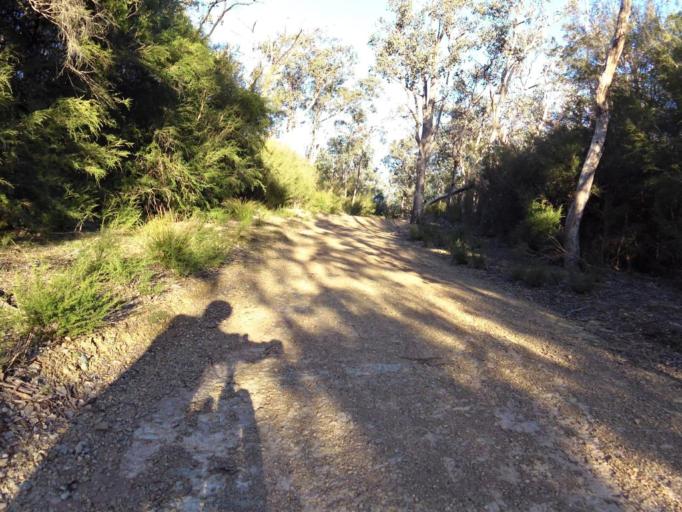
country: AU
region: Victoria
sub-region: Nillumbik
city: North Warrandyte
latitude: -37.7222
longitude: 145.2368
